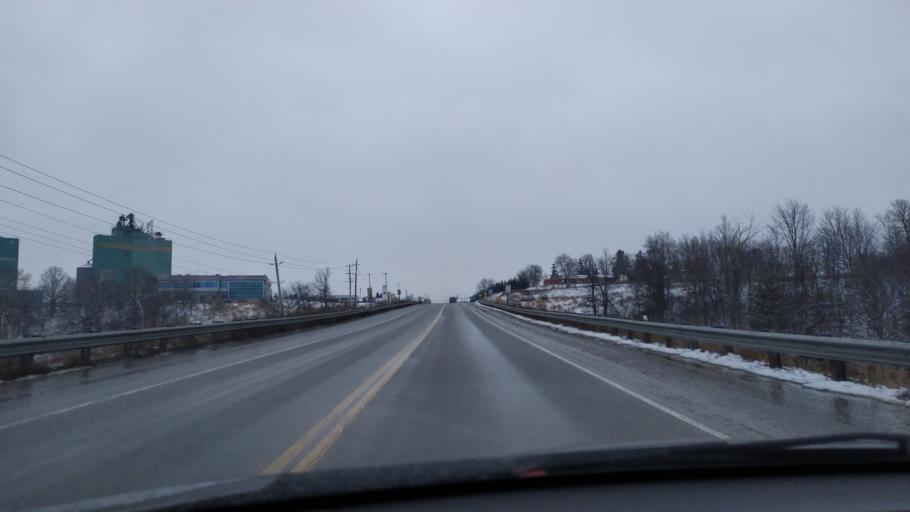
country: CA
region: Ontario
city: Waterloo
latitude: 43.6025
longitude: -80.6415
